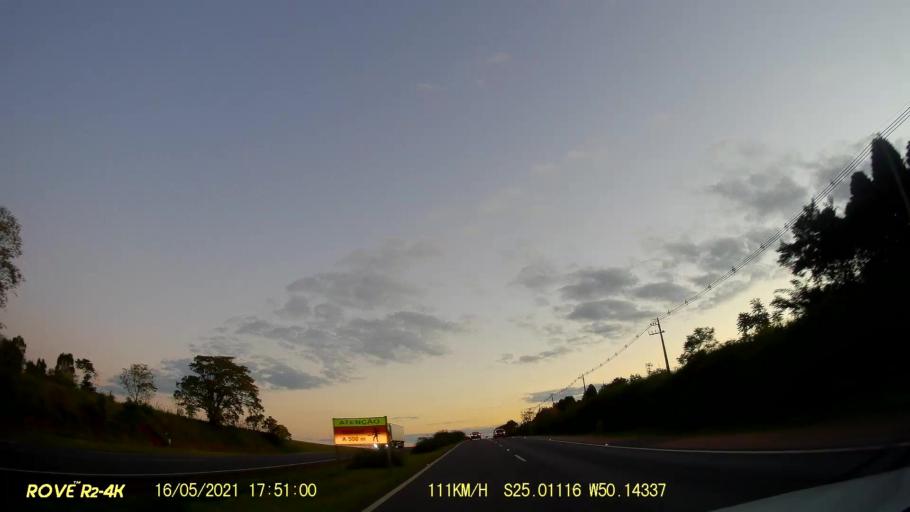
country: BR
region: Parana
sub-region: Carambei
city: Carambei
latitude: -25.0118
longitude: -50.1439
